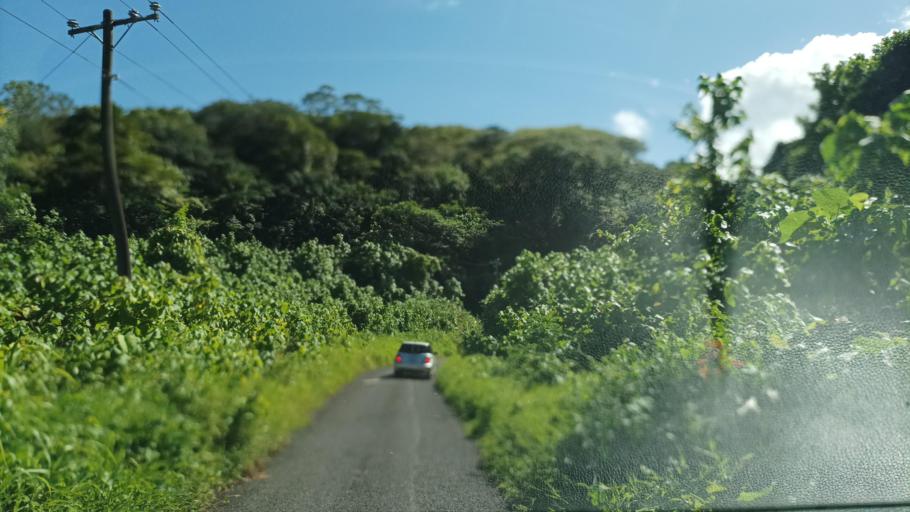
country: FM
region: Pohnpei
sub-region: Madolenihm Municipality
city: Madolenihm Municipality Government
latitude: 6.8430
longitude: 158.3124
